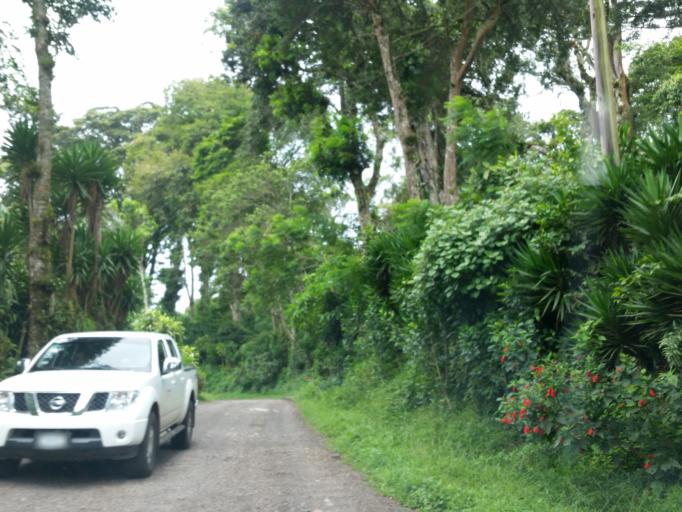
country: NI
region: Matagalpa
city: Matagalpa
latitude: 12.9986
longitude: -85.9128
